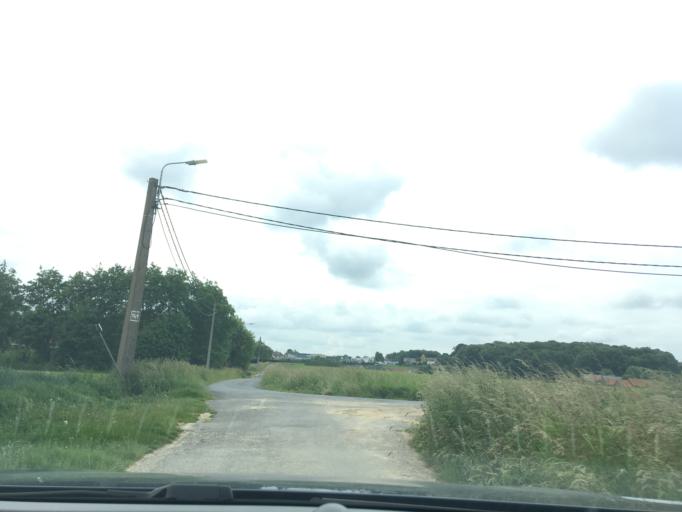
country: BE
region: Wallonia
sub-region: Province du Hainaut
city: Mouscron
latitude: 50.7649
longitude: 3.1910
